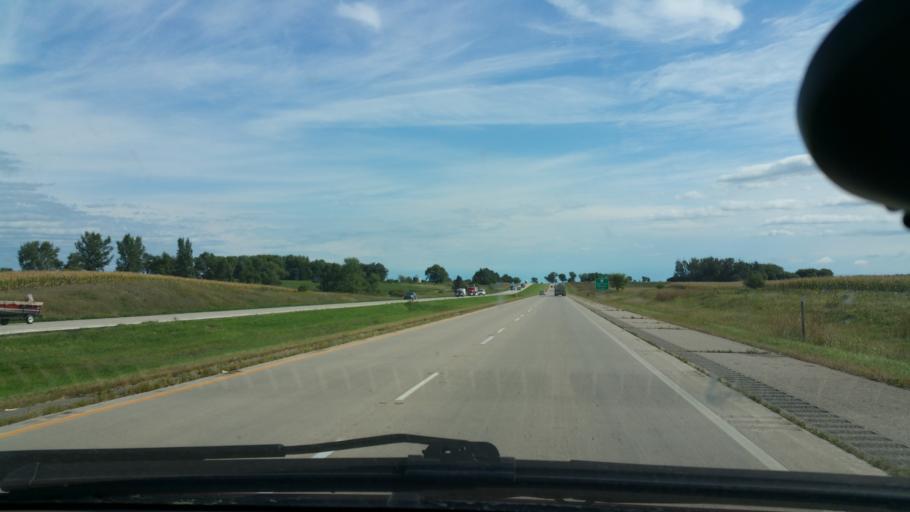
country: US
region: Minnesota
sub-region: Freeborn County
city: Albert Lea
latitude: 43.8004
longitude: -93.2976
